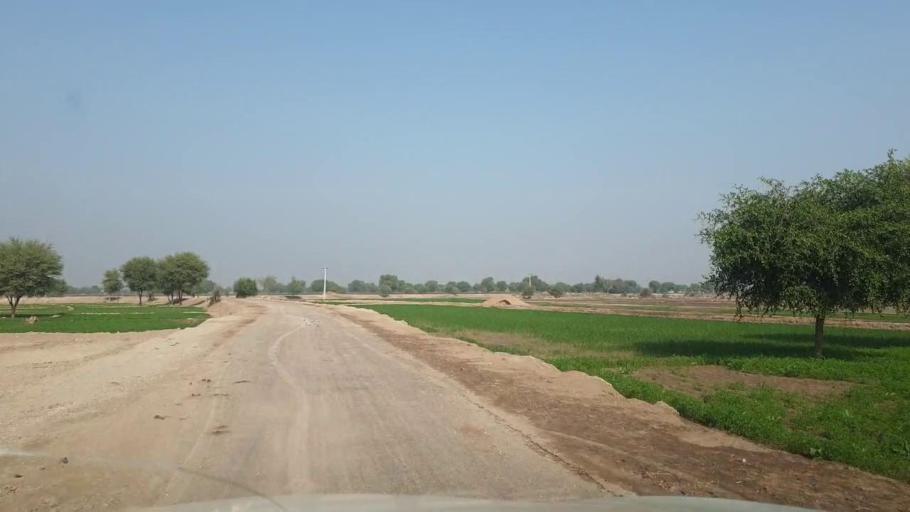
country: PK
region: Sindh
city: Bhan
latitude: 26.5095
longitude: 67.7964
